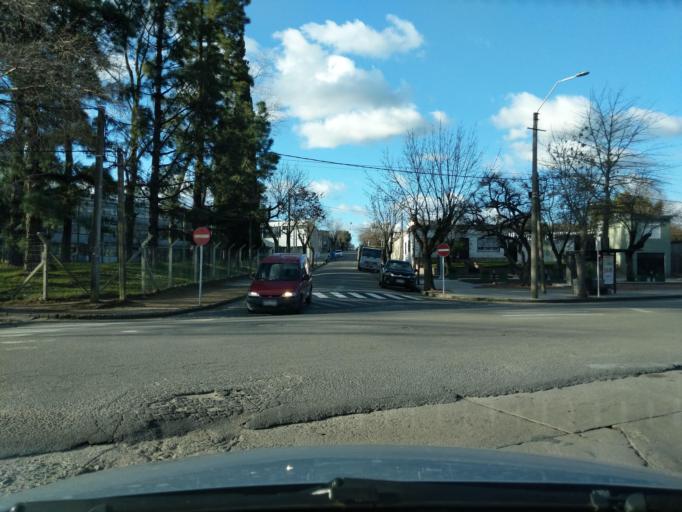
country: UY
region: Florida
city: Florida
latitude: -34.1000
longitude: -56.2221
